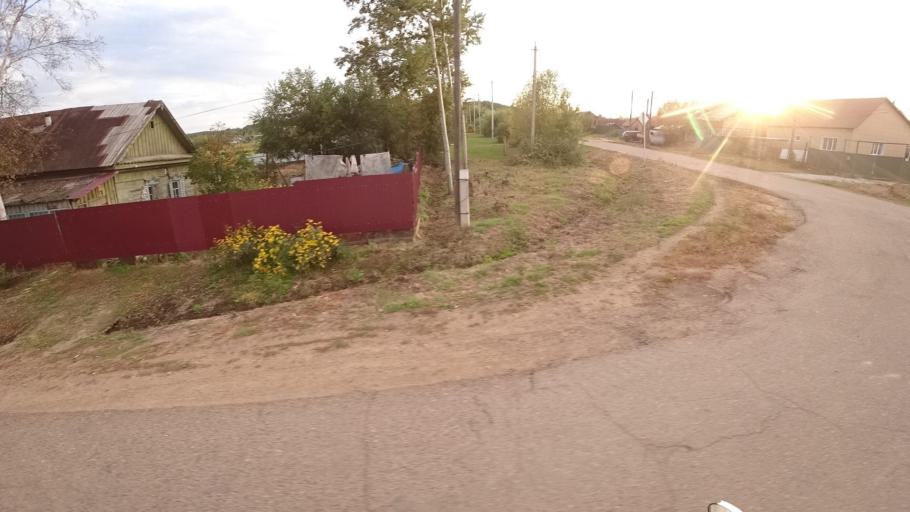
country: RU
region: Primorskiy
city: Yakovlevka
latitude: 44.4225
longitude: 133.4717
